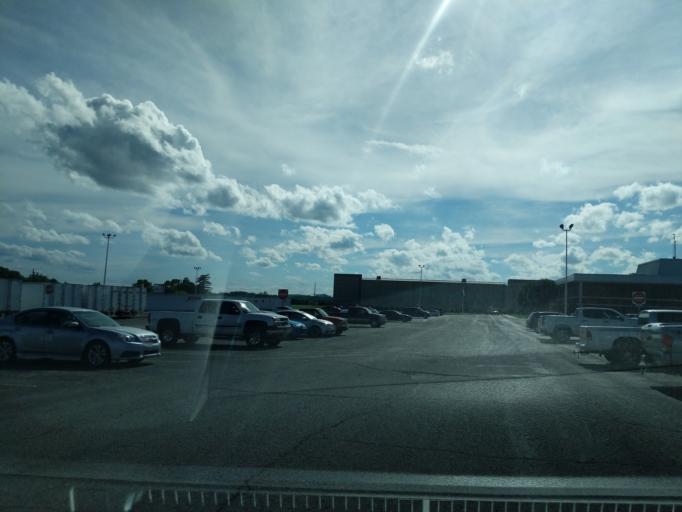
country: US
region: Tennessee
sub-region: Davidson County
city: Lakewood
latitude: 36.2681
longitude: -86.6543
